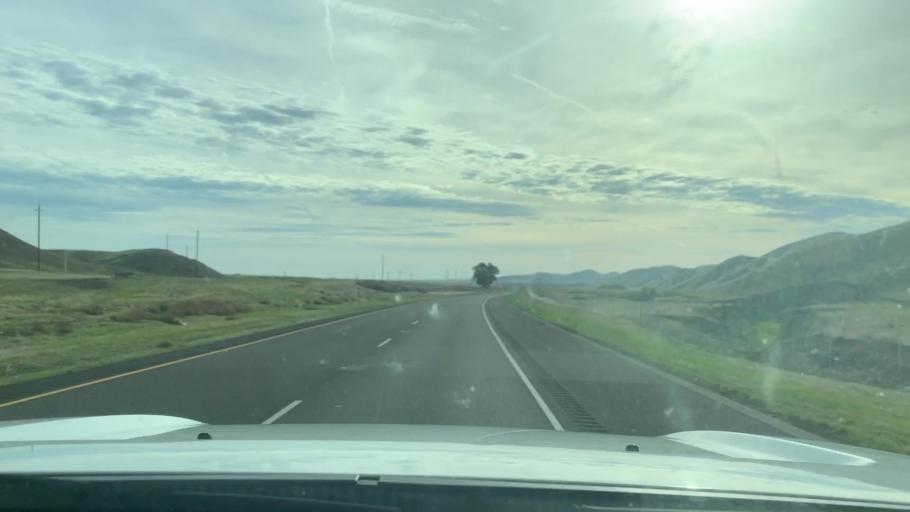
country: US
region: California
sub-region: San Luis Obispo County
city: Shandon
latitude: 35.7146
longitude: -120.1725
